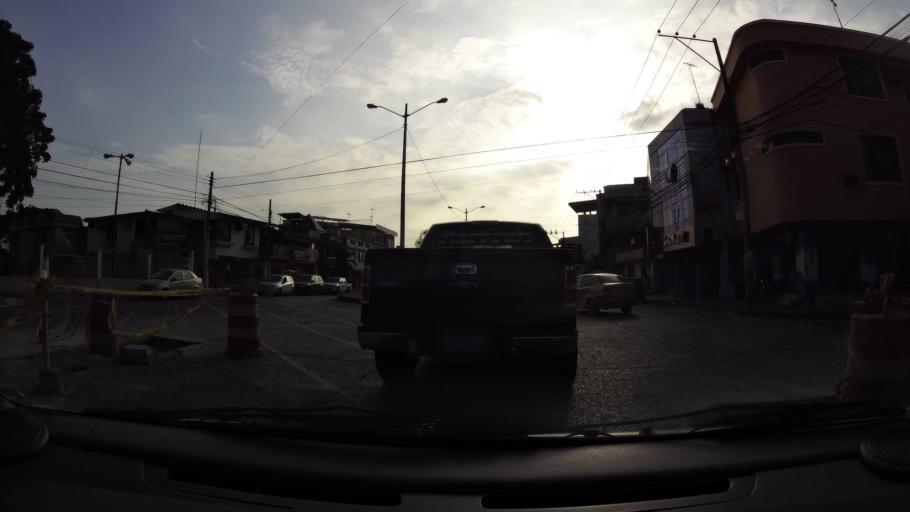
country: EC
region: Guayas
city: Eloy Alfaro
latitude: -2.1330
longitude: -79.9057
